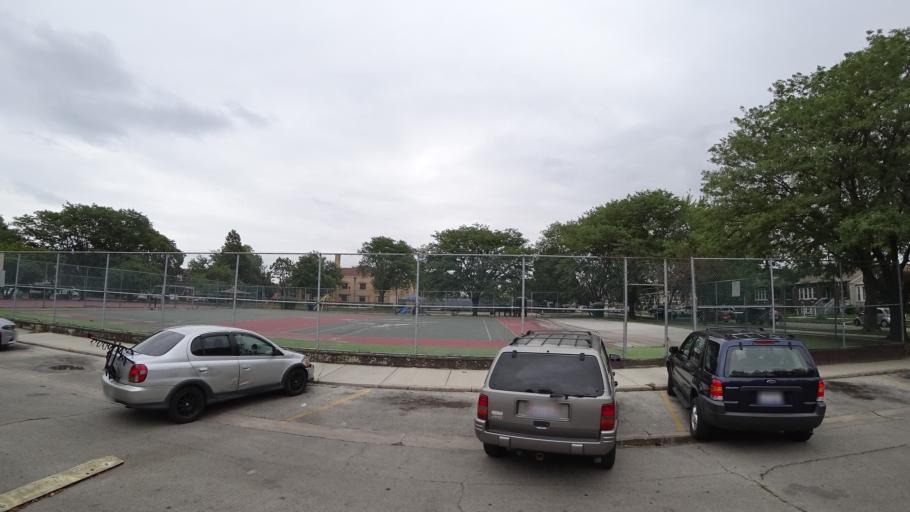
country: US
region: Illinois
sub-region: Cook County
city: Cicero
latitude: 41.8567
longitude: -87.7526
